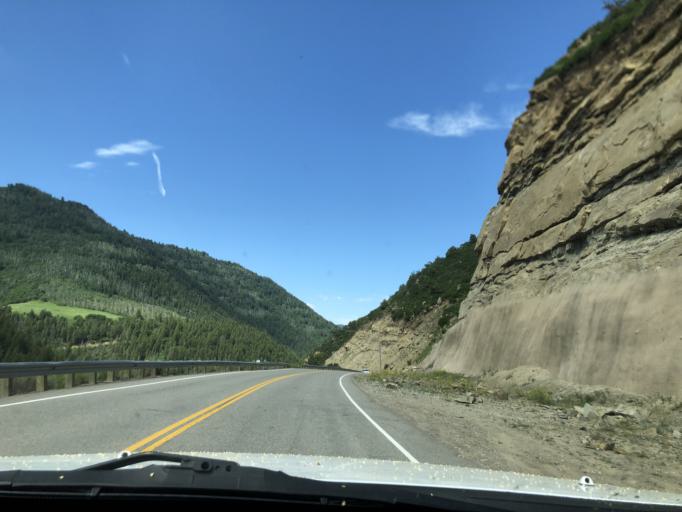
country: US
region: Colorado
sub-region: Delta County
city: Paonia
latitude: 38.9431
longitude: -107.3529
